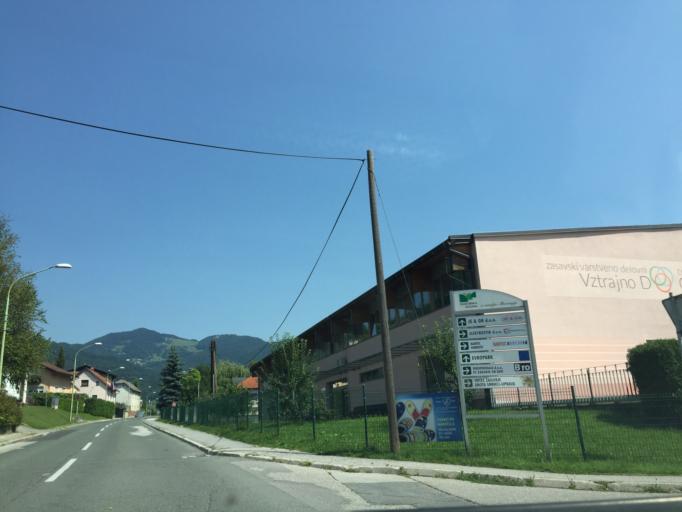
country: SI
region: Zagorje ob Savi
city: Zagorje ob Savi
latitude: 46.1354
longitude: 15.0020
